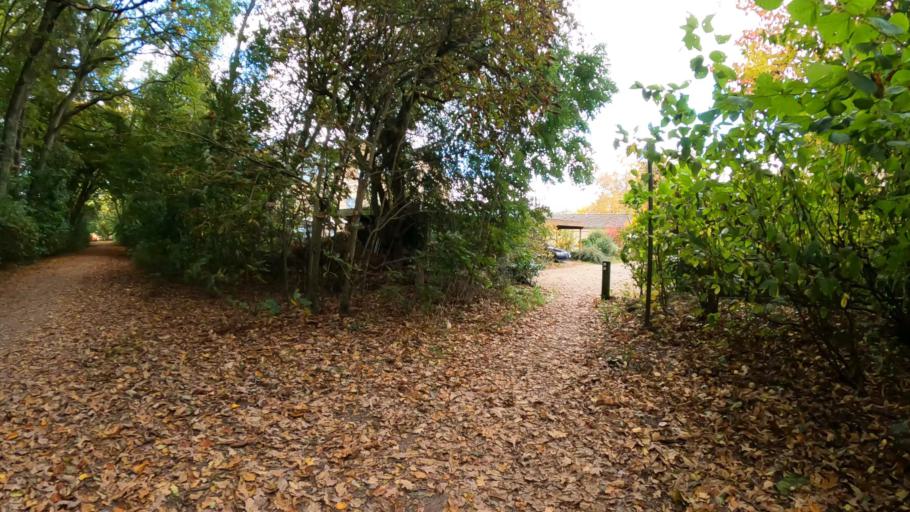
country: DE
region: Schleswig-Holstein
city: Delingsdorf
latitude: 53.6885
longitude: 10.2492
